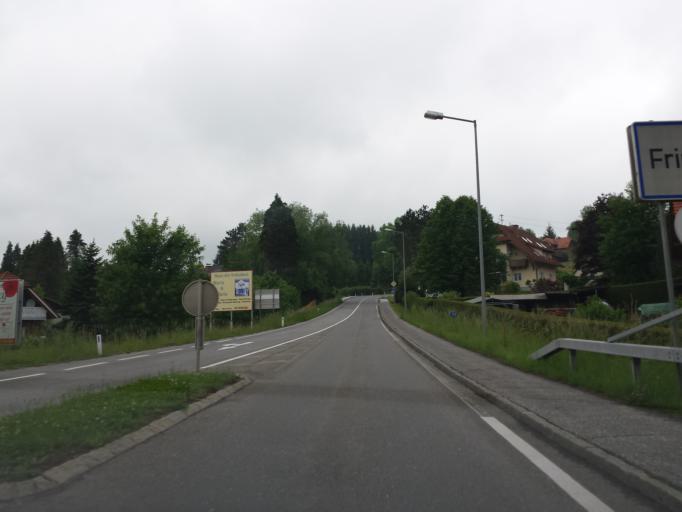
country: AT
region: Styria
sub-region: Politischer Bezirk Graz-Umgebung
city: Kumberg
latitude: 47.1505
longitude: 15.5483
